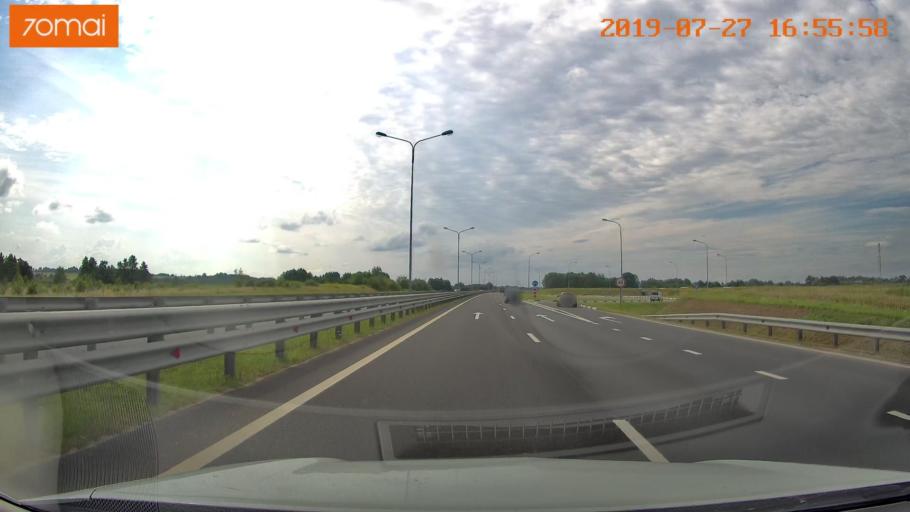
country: RU
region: Kaliningrad
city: Bol'shoe Isakovo
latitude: 54.6927
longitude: 20.7546
